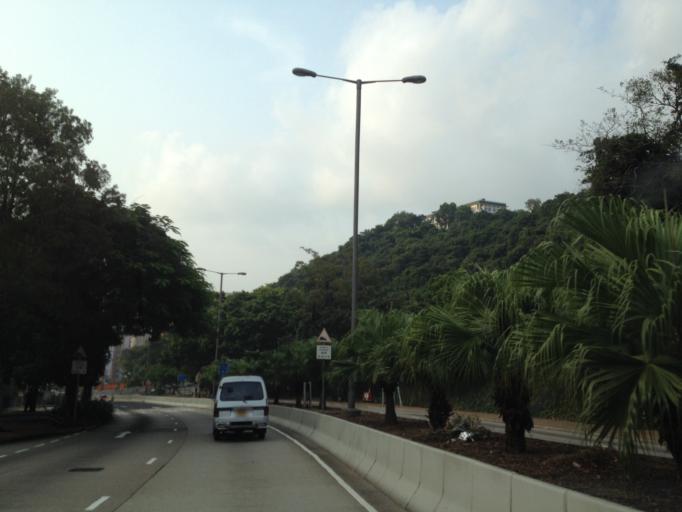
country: HK
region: Wanchai
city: Wan Chai
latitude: 22.2725
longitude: 114.2327
